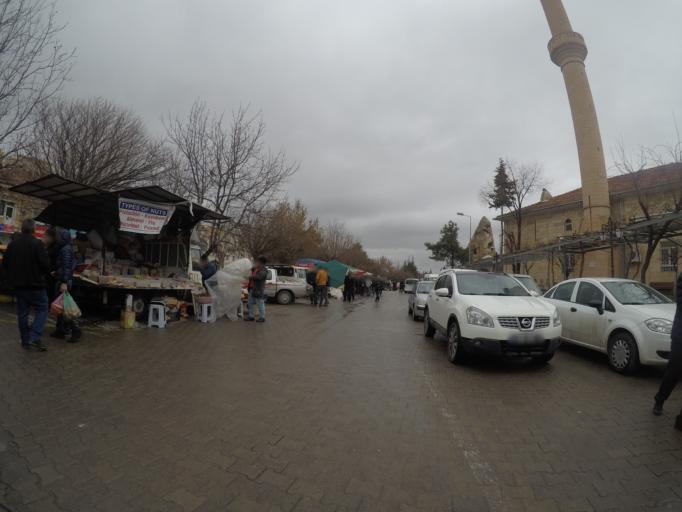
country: TR
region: Nevsehir
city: Goereme
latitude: 38.6415
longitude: 34.8291
